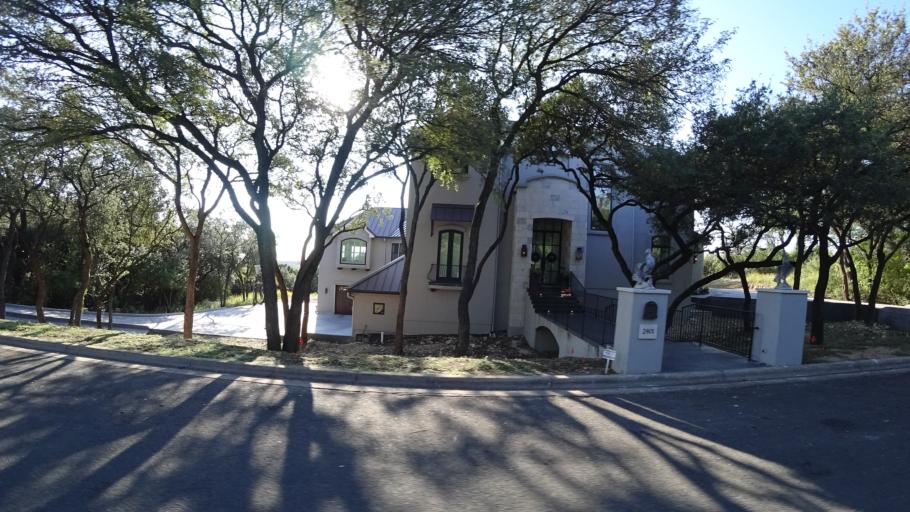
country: US
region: Texas
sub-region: Travis County
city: Rollingwood
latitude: 30.2642
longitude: -97.7953
